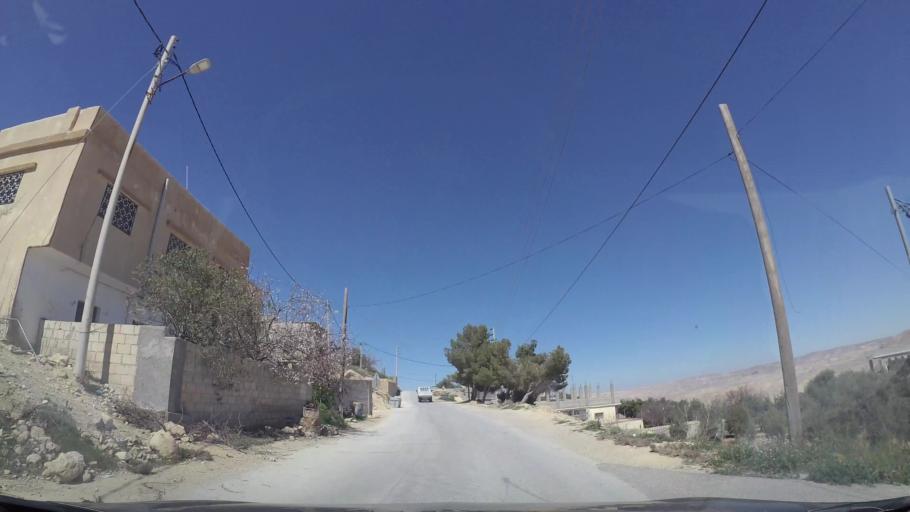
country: JO
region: Tafielah
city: At Tafilah
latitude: 30.8377
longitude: 35.5747
